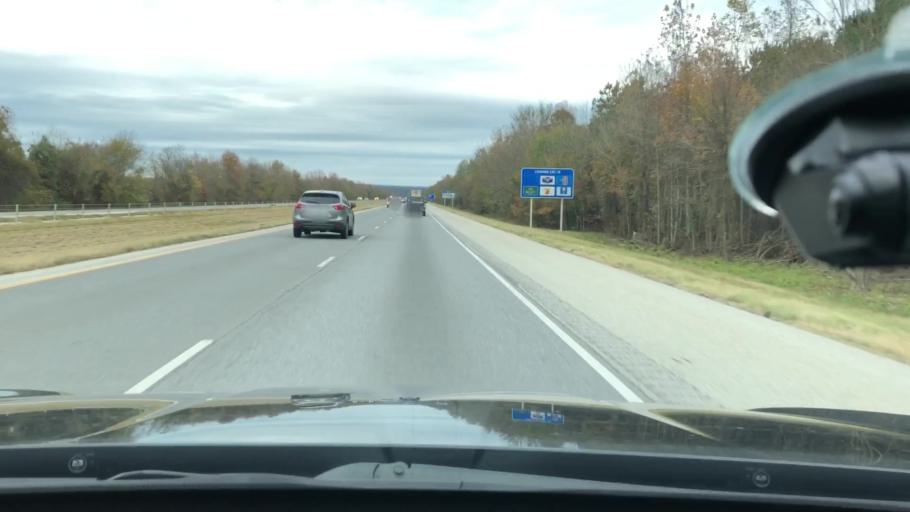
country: US
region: Arkansas
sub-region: Clark County
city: Arkadelphia
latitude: 34.1584
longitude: -93.0771
